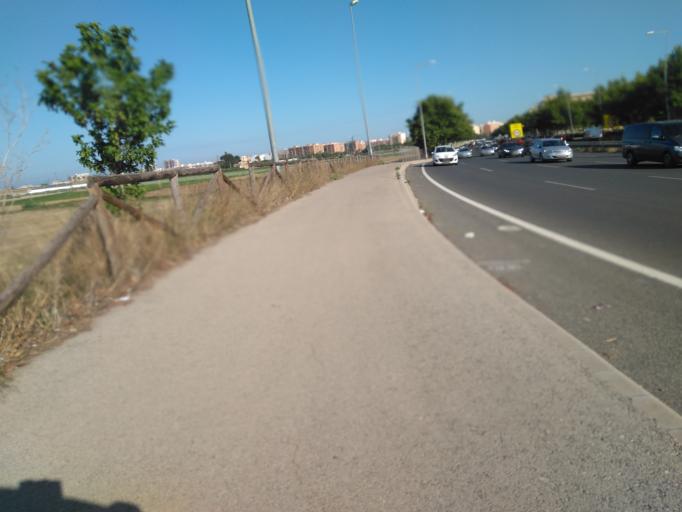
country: ES
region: Valencia
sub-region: Provincia de Valencia
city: Tavernes Blanques
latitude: 39.5028
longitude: -0.3916
